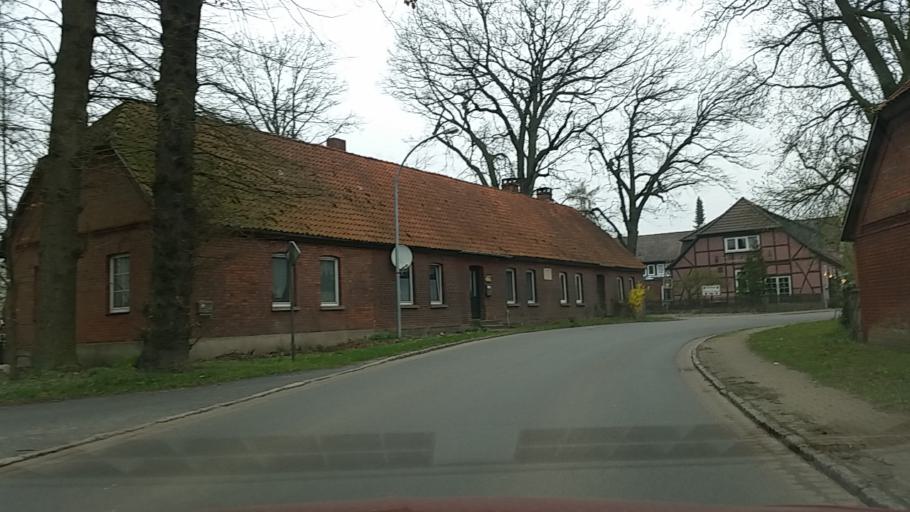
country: DE
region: Lower Saxony
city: Suderburg
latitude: 52.9354
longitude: 10.4838
